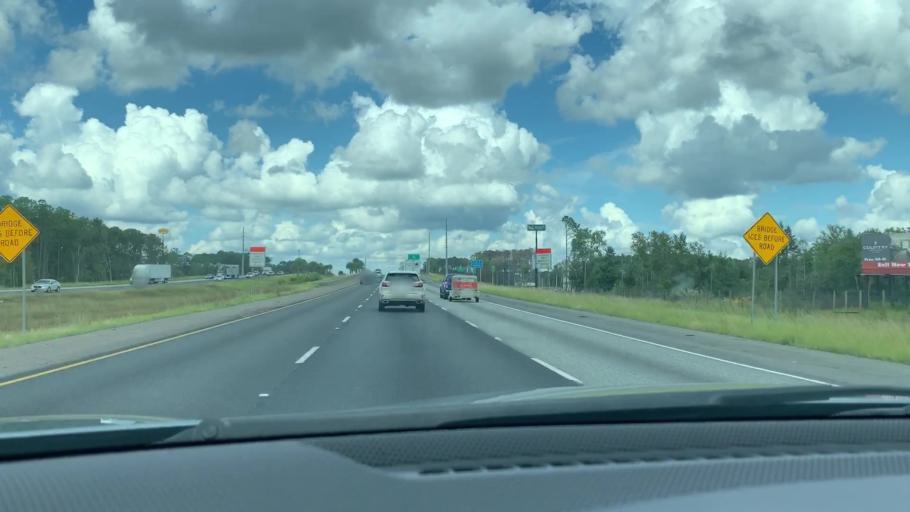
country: US
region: Georgia
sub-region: Camden County
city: Kingsland
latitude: 30.7863
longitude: -81.6578
